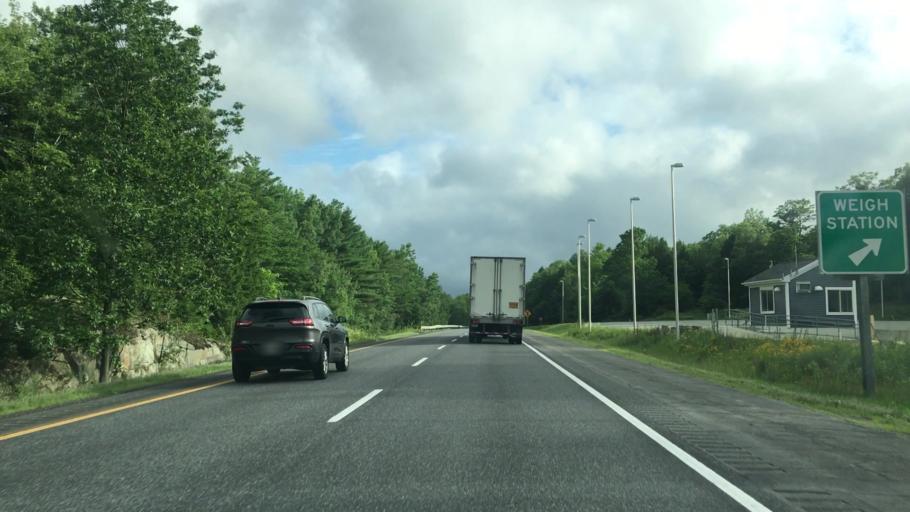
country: US
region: Maine
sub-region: Kennebec County
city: Sidney
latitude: 44.4042
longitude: -69.7511
